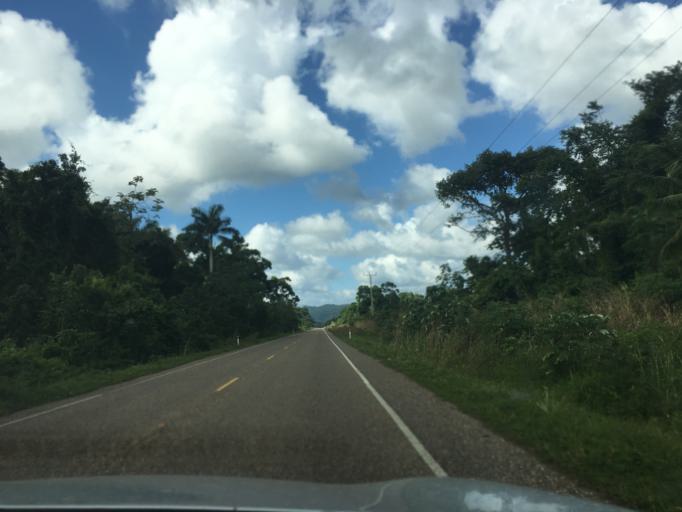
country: BZ
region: Stann Creek
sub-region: Dangriga
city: Dangriga
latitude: 16.8546
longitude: -88.3276
